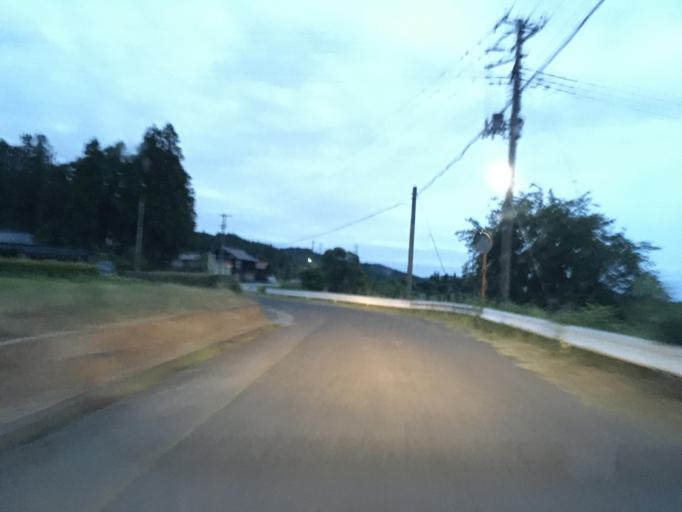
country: JP
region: Miyagi
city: Furukawa
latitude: 38.7706
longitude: 140.8921
